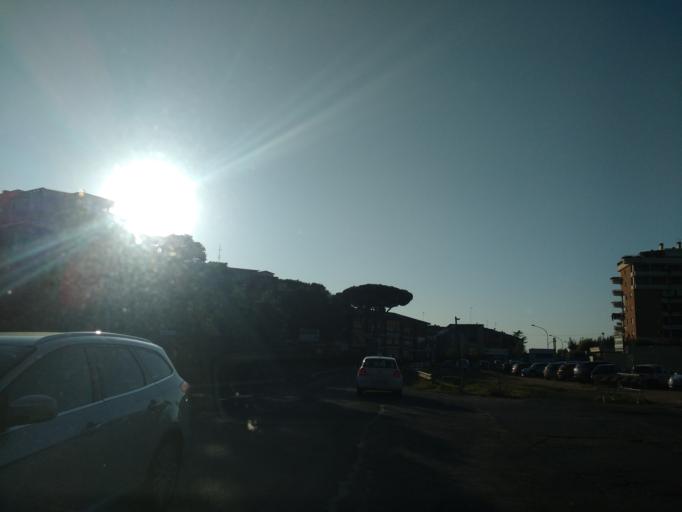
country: IT
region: Latium
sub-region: Citta metropolitana di Roma Capitale
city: Vitinia
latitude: 41.7699
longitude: 12.3746
